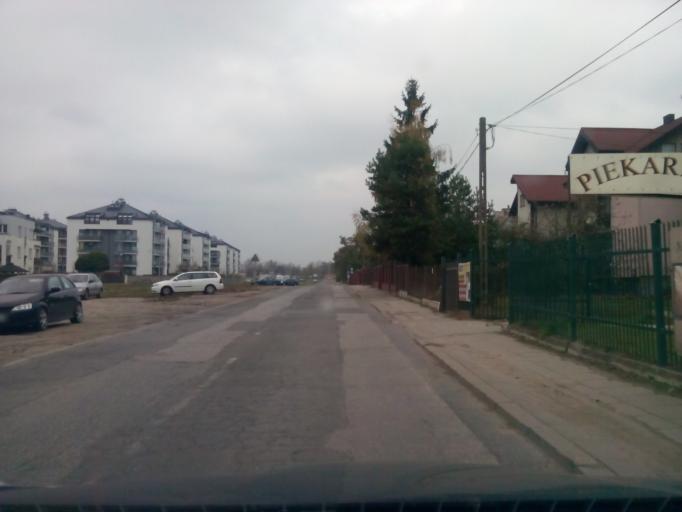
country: PL
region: Masovian Voivodeship
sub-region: Powiat pruszkowski
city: Pruszkow
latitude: 52.1580
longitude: 20.7842
